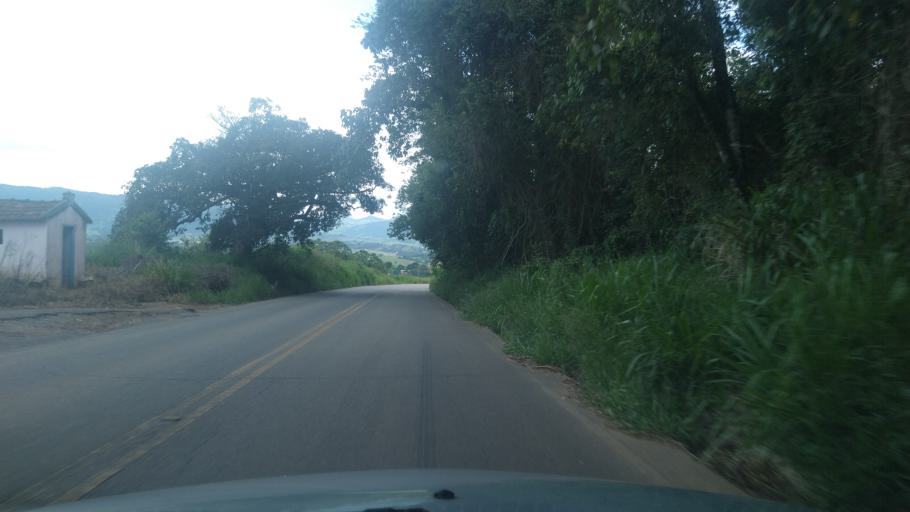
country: BR
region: Minas Gerais
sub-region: Extrema
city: Extrema
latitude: -22.7860
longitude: -46.3203
